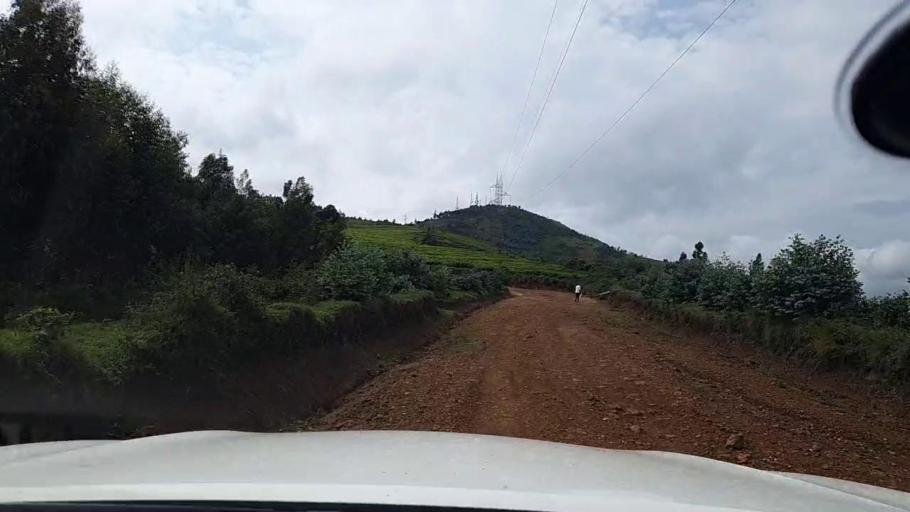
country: RW
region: Western Province
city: Kibuye
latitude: -2.1355
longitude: 29.3755
